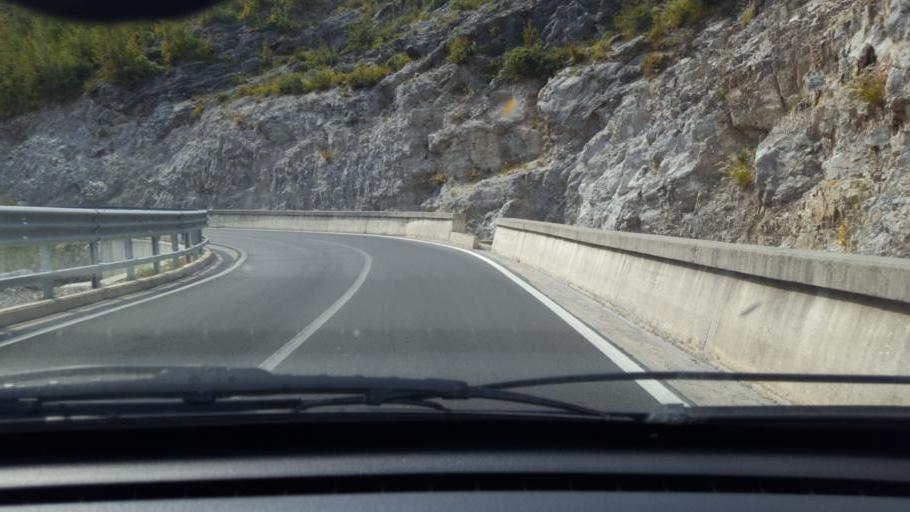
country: AL
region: Shkoder
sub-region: Rrethi i Malesia e Madhe
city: Kastrat
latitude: 42.4197
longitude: 19.5045
